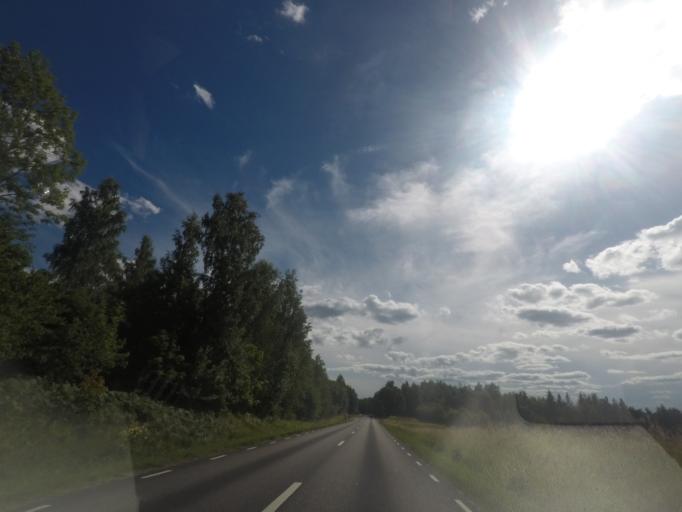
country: SE
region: Stockholm
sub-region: Norrtalje Kommun
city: Arno
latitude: 60.0050
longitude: 18.8015
